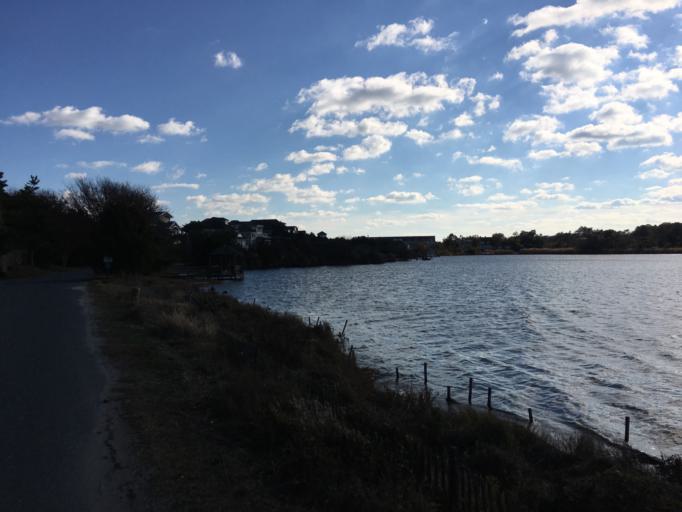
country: US
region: Delaware
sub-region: Sussex County
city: Rehoboth Beach
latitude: 38.7071
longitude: -75.0764
